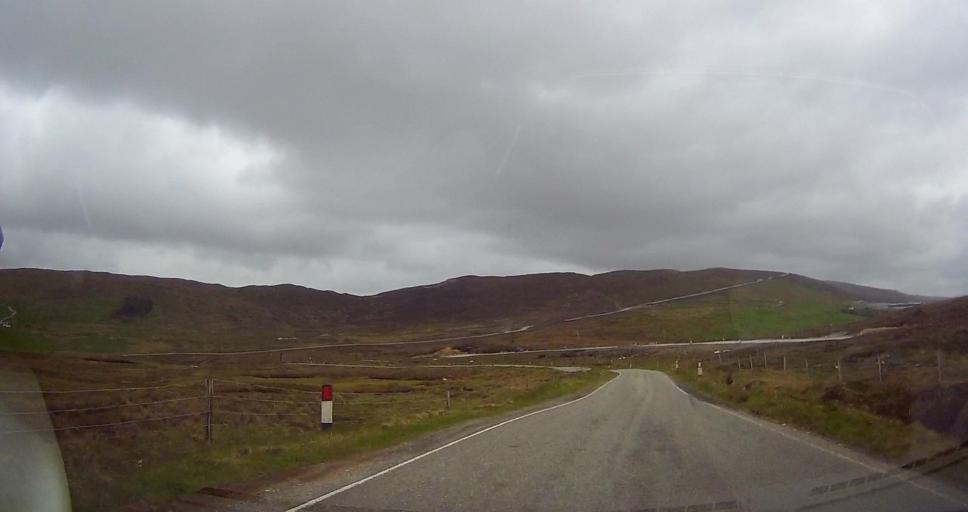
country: GB
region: Scotland
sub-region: Shetland Islands
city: Lerwick
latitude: 60.2774
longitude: -1.2644
